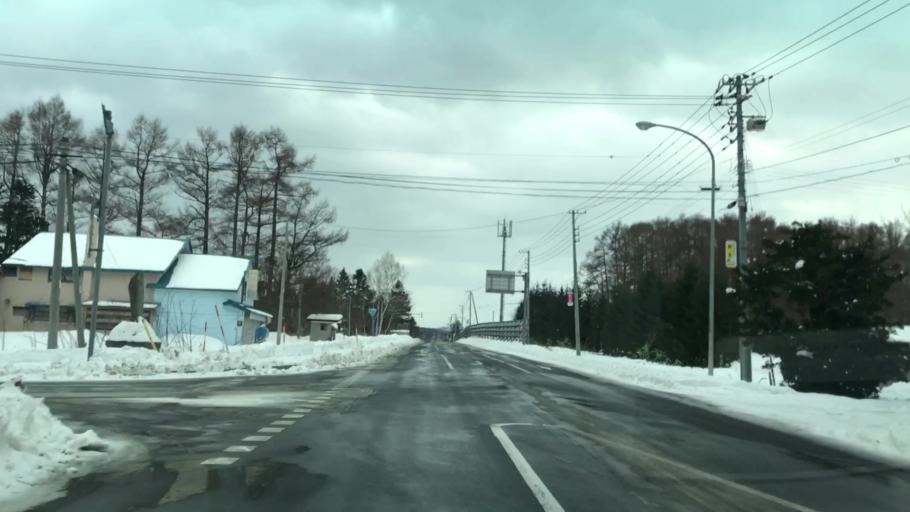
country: JP
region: Hokkaido
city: Yoichi
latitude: 43.3135
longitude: 140.5441
